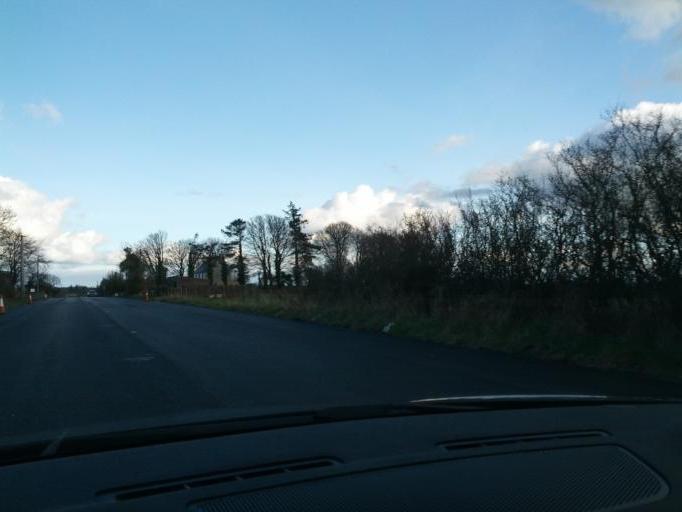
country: IE
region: Connaught
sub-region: Roscommon
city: Castlerea
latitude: 53.6888
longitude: -8.4039
